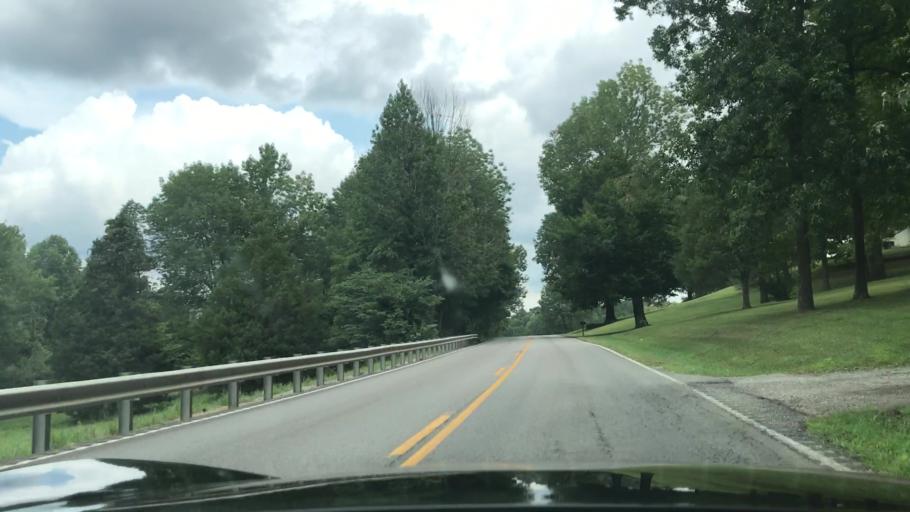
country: US
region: Kentucky
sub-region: Muhlenberg County
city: Central City
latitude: 37.2060
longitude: -87.0752
